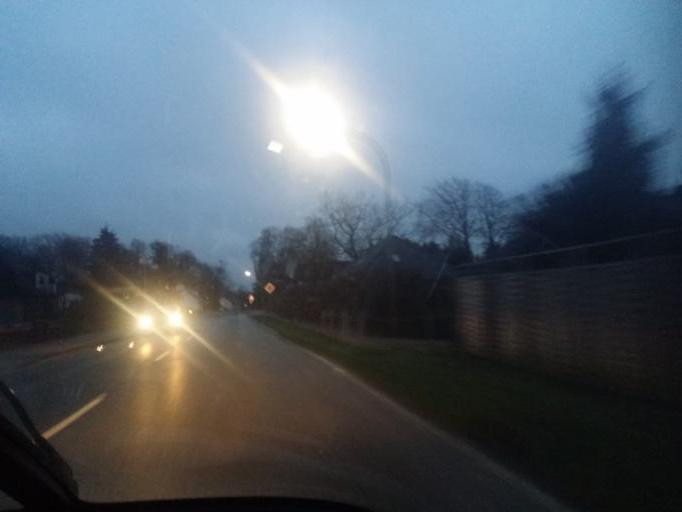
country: DE
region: Schleswig-Holstein
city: Schenefeld
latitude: 54.0520
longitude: 9.4798
